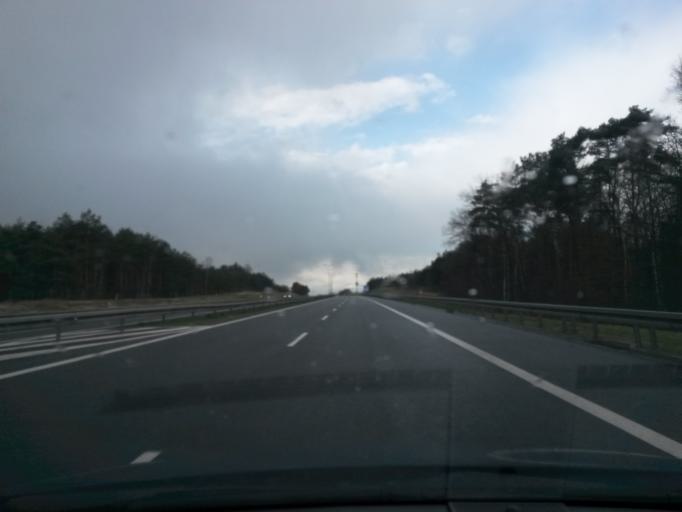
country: PL
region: Greater Poland Voivodeship
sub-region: Powiat koninski
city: Golina
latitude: 52.1776
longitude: 18.1334
